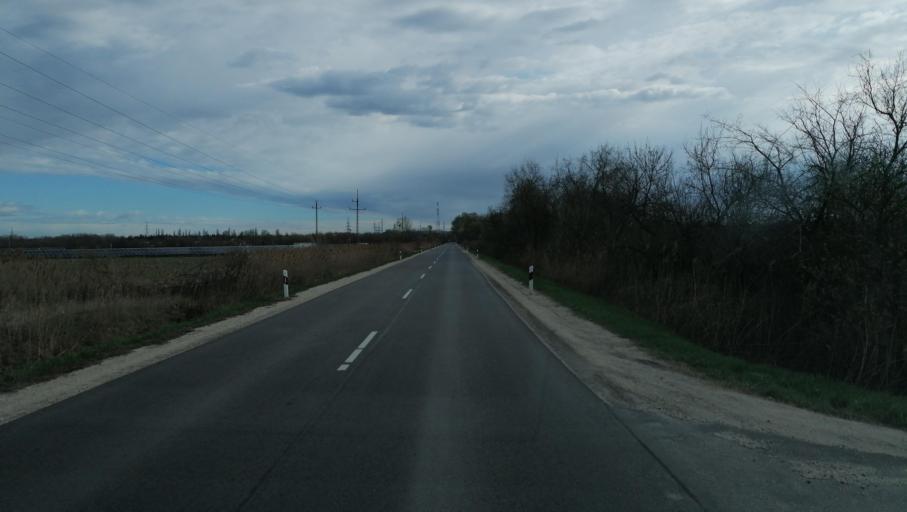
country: HU
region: Pest
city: Ocsa
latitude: 47.2539
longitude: 19.2117
